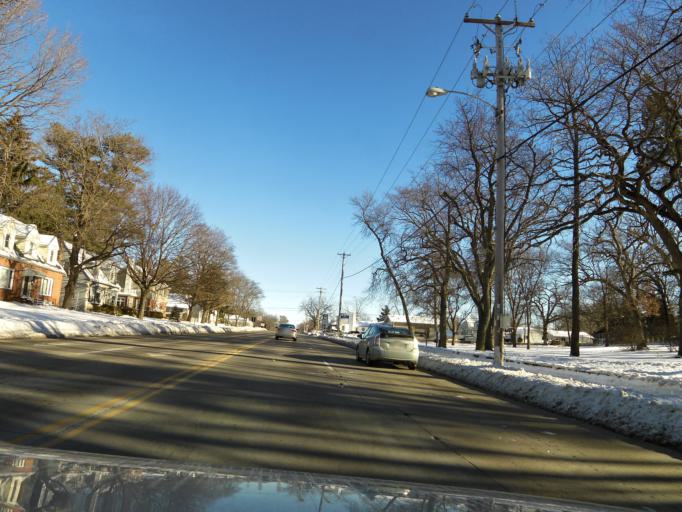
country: US
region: Wisconsin
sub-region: Sauk County
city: Baraboo
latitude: 43.4748
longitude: -89.7544
